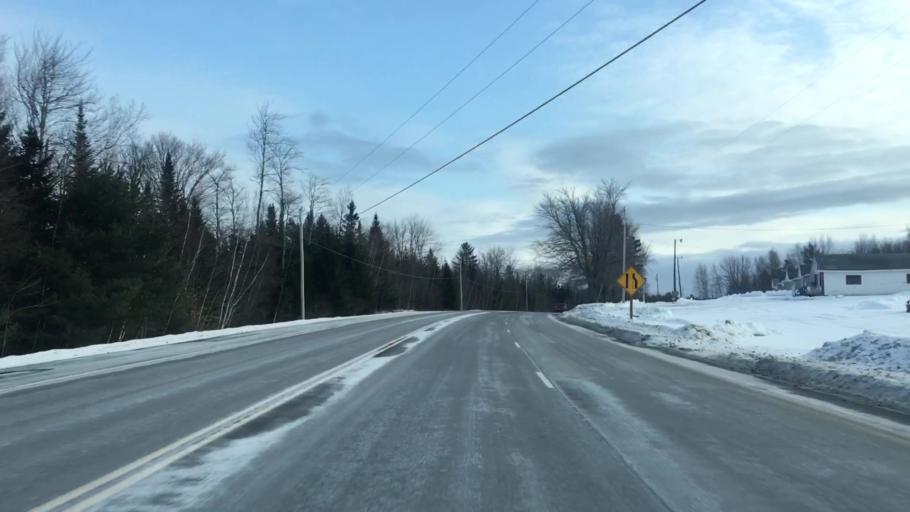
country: US
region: Maine
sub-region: Washington County
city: Machias
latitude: 44.9476
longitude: -67.6983
